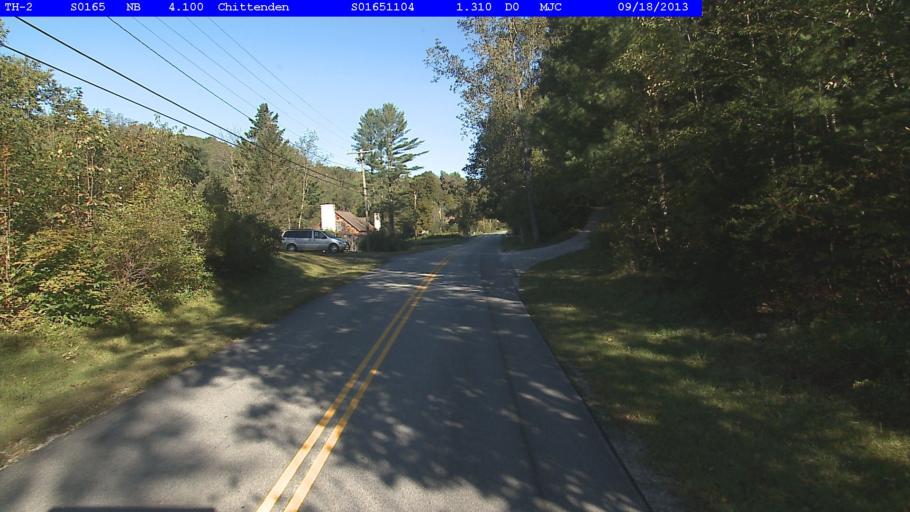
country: US
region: Vermont
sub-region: Rutland County
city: Rutland
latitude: 43.6950
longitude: -72.9560
